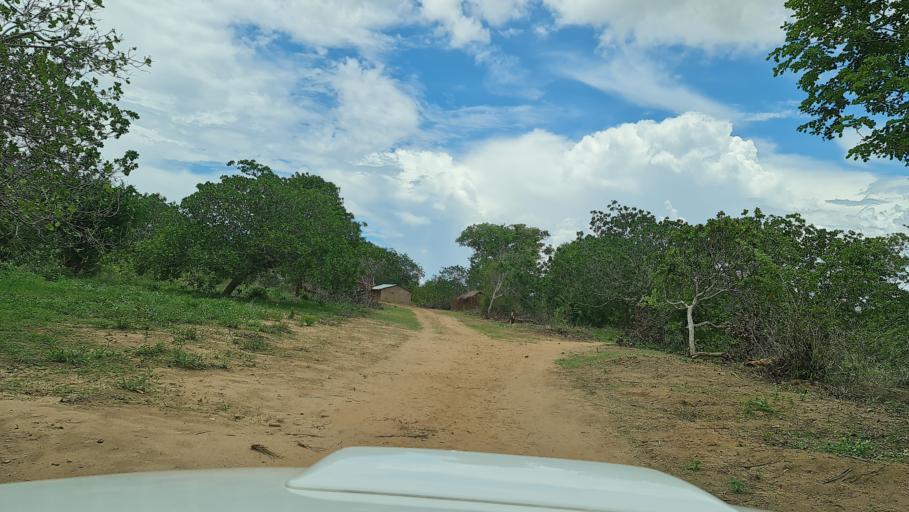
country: MZ
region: Nampula
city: Ilha de Mocambique
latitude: -15.5143
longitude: 40.2027
